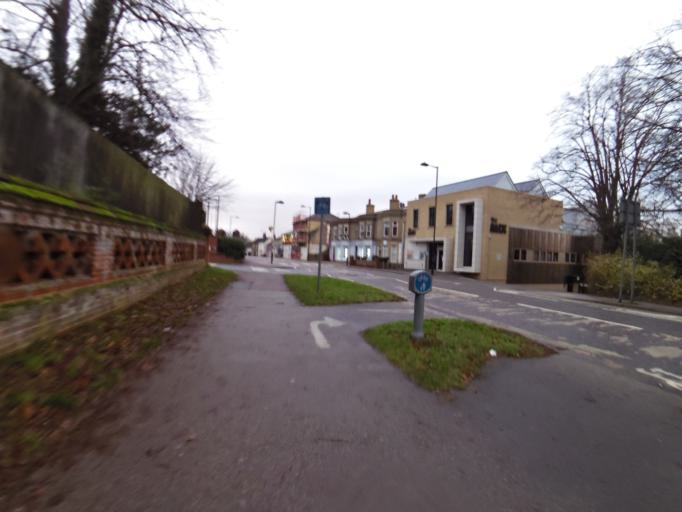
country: GB
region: England
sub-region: Suffolk
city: Stowmarket
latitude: 52.1848
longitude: 0.9994
